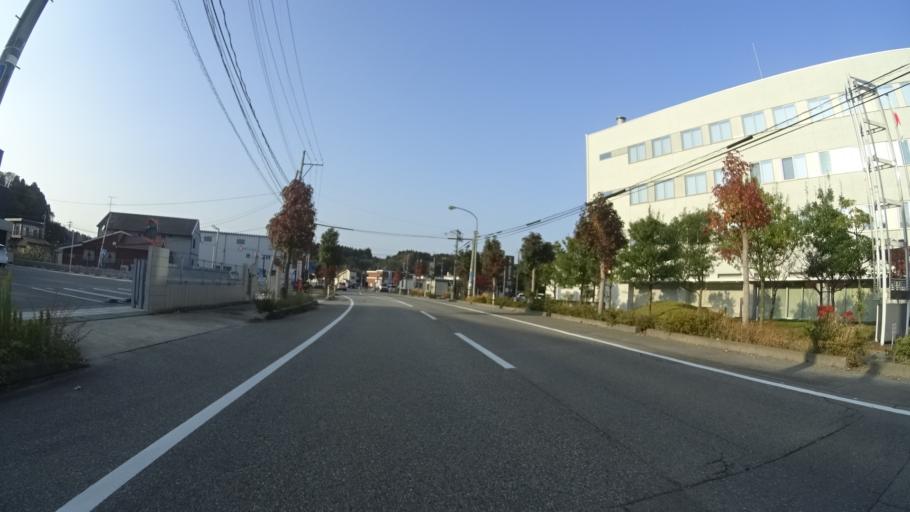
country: JP
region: Ishikawa
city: Nanao
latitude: 37.0547
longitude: 136.9547
